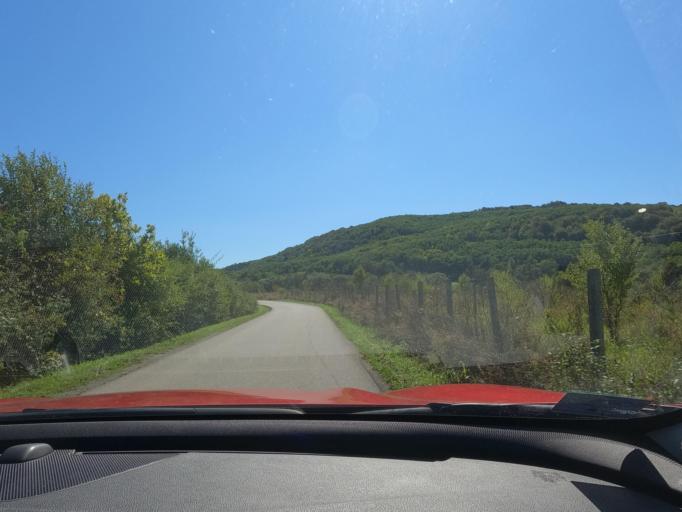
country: HR
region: Sisacko-Moslavacka
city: Petrinja
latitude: 45.4170
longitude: 16.2550
